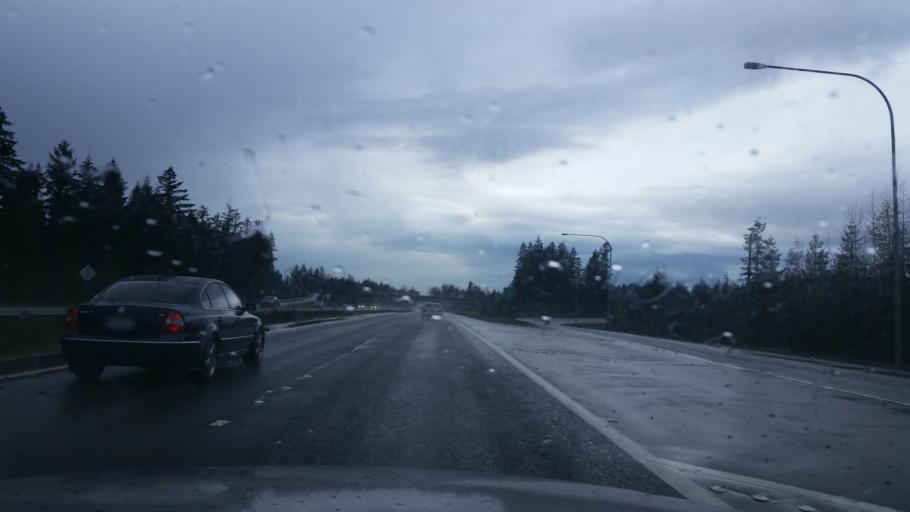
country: US
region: Washington
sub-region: King County
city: Covington
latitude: 47.3753
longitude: -122.0871
